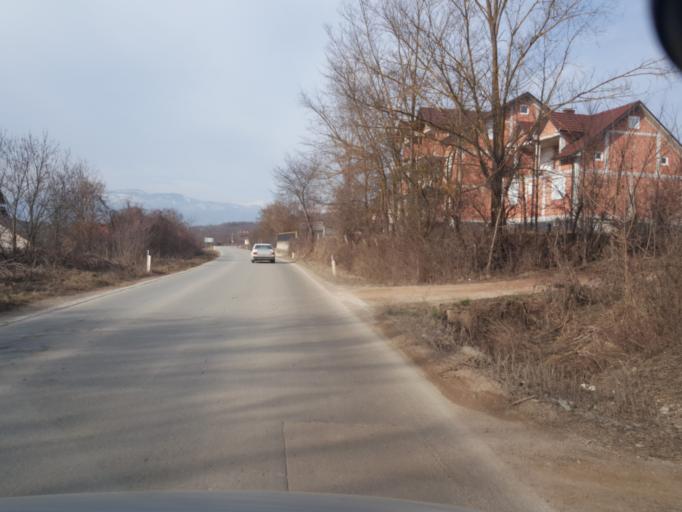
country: XK
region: Pec
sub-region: Komuna e Klines
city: Klina
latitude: 42.6651
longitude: 20.5381
